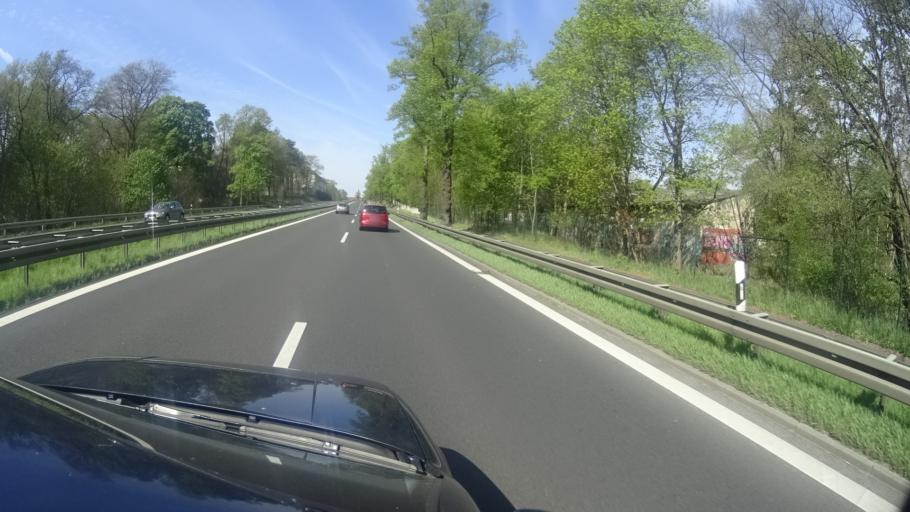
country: DE
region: Brandenburg
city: Dallgow-Doeberitz
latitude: 52.5334
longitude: 13.0153
